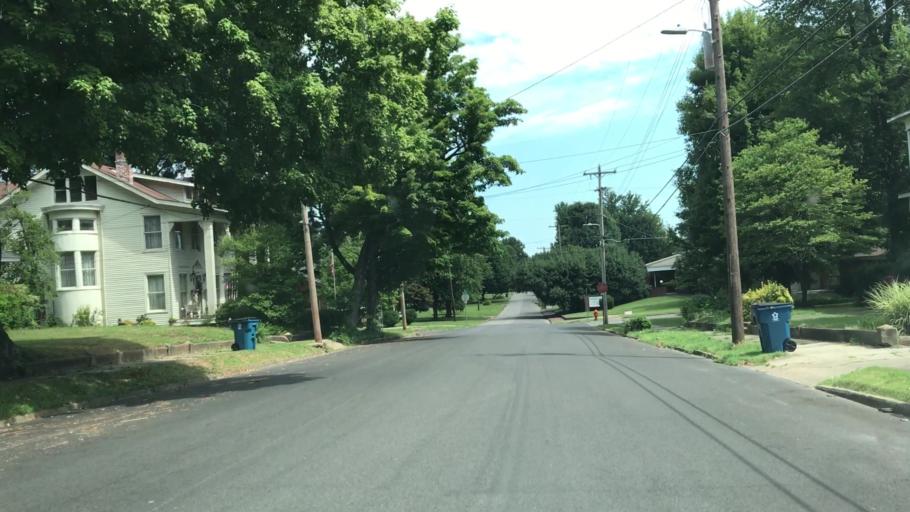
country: US
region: Kentucky
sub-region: Graves County
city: Mayfield
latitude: 36.7447
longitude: -88.6333
